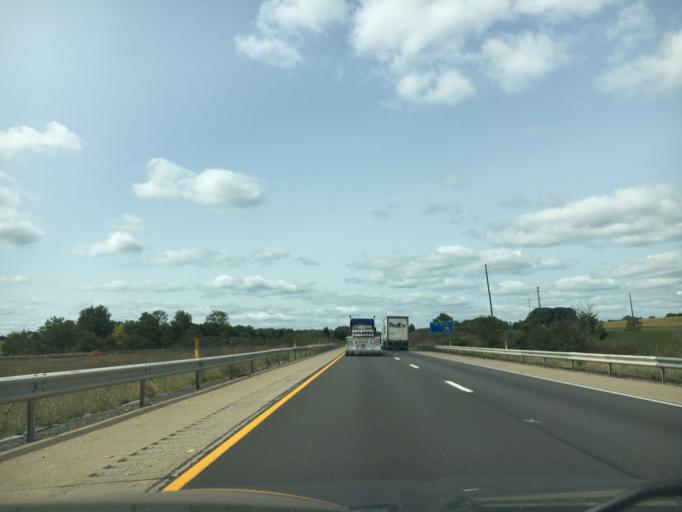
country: US
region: Pennsylvania
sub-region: Northumberland County
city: Milton
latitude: 41.0103
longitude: -76.7764
